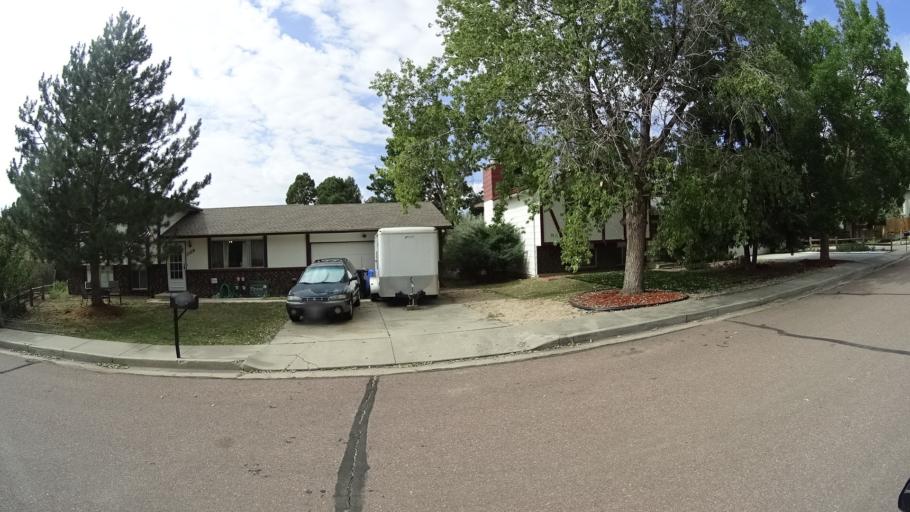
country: US
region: Colorado
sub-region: El Paso County
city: Cimarron Hills
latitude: 38.8482
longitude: -104.7246
